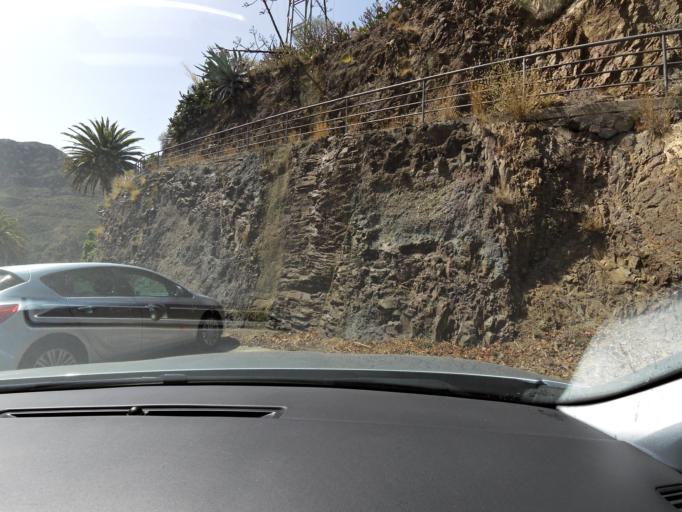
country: ES
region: Canary Islands
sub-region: Provincia de Santa Cruz de Tenerife
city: Santiago del Teide
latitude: 28.3053
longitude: -16.8399
